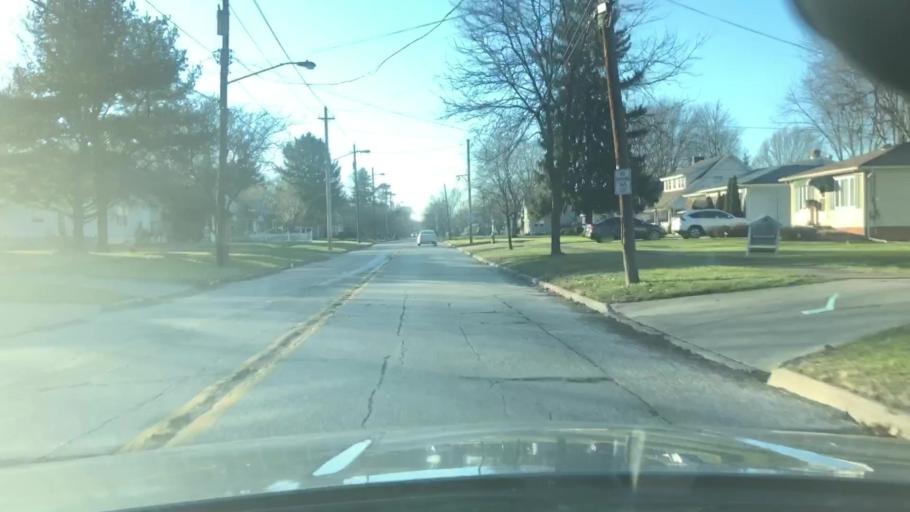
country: US
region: Ohio
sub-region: Cuyahoga County
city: Berea
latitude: 41.3646
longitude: -81.8650
